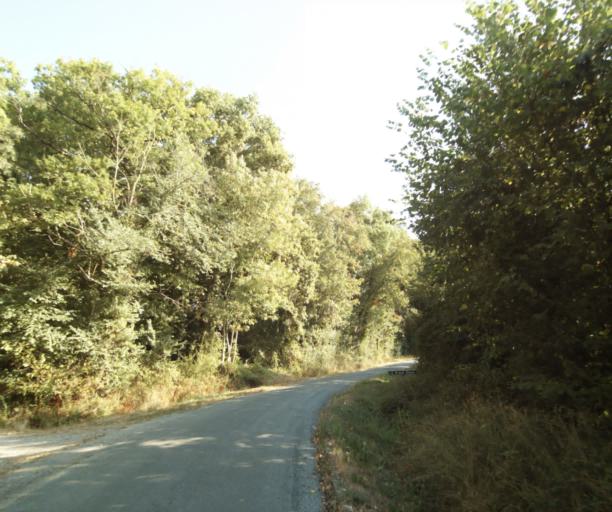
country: FR
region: Poitou-Charentes
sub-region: Departement de la Charente-Maritime
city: Cabariot
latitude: 45.9602
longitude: -0.8427
